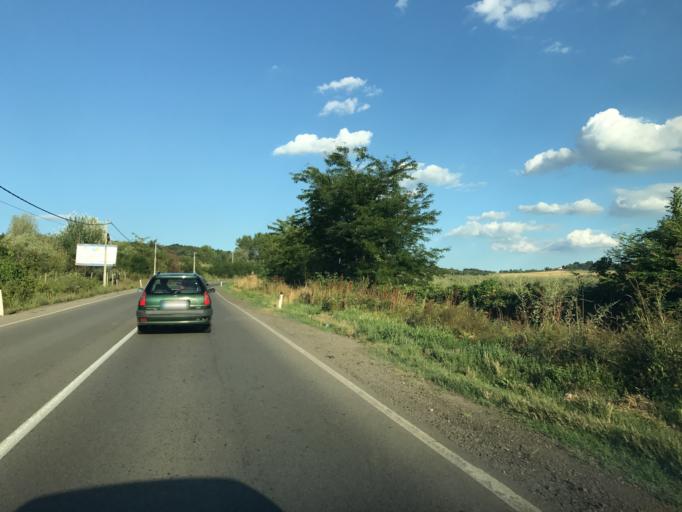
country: RS
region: Central Serbia
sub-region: Belgrade
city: Grocka
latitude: 44.7194
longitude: 20.6444
